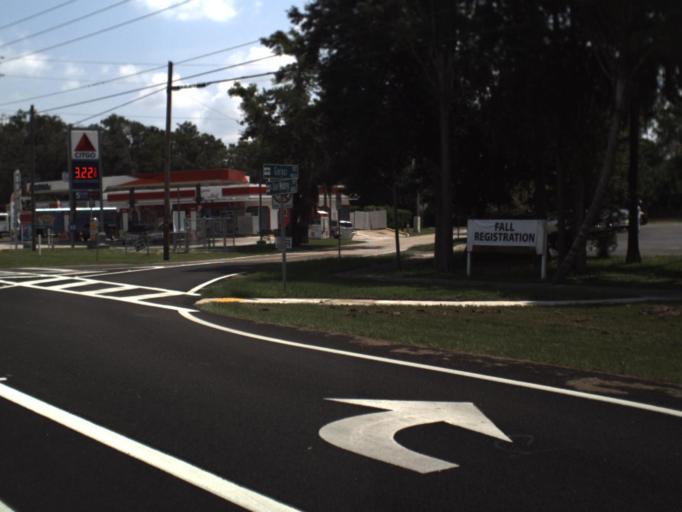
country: US
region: Florida
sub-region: Hillsborough County
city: Cheval
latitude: 28.1500
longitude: -82.4931
